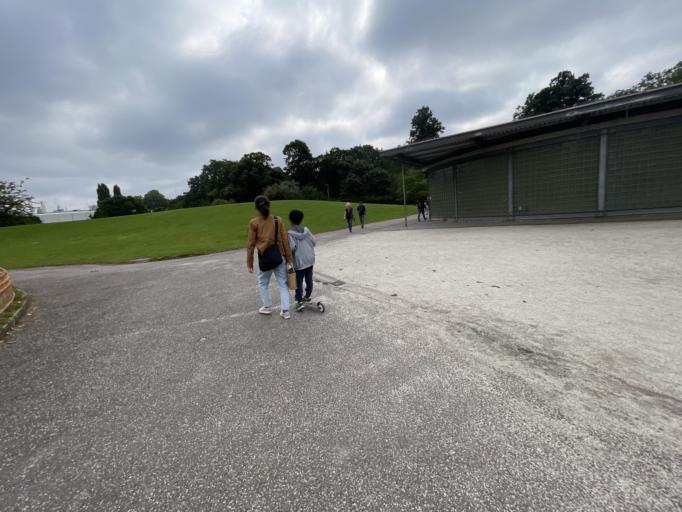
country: GB
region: England
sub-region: Greater London
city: Battersea
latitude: 51.4801
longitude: -0.1594
